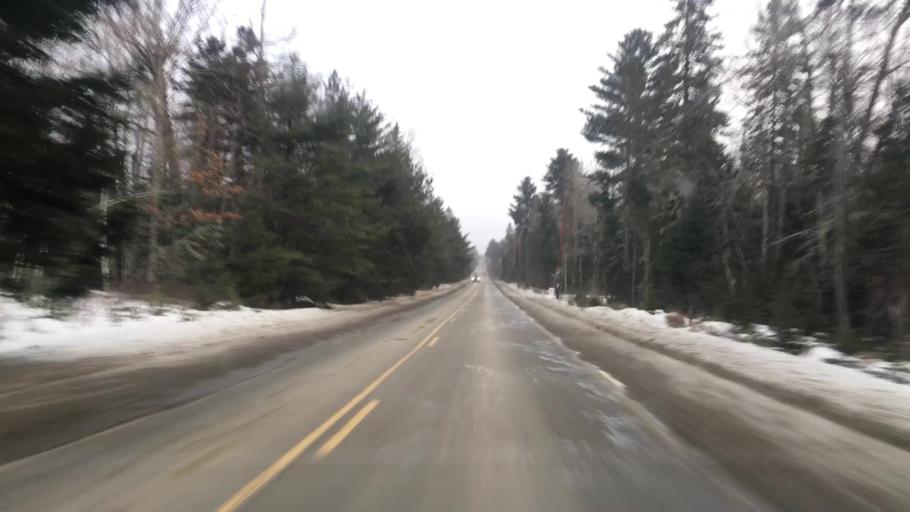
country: US
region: Maine
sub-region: Hancock County
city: Ellsworth
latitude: 44.6675
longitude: -68.3552
